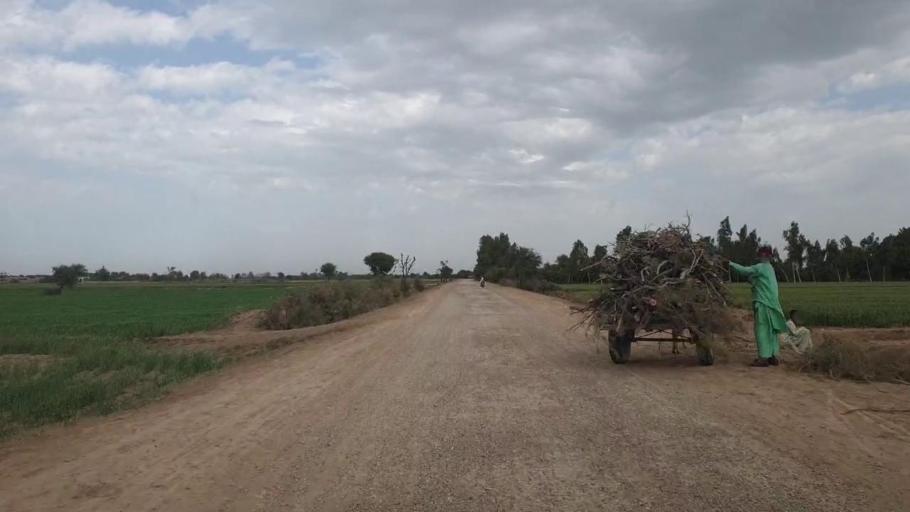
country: PK
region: Sindh
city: Hala
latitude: 25.9307
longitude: 68.3904
